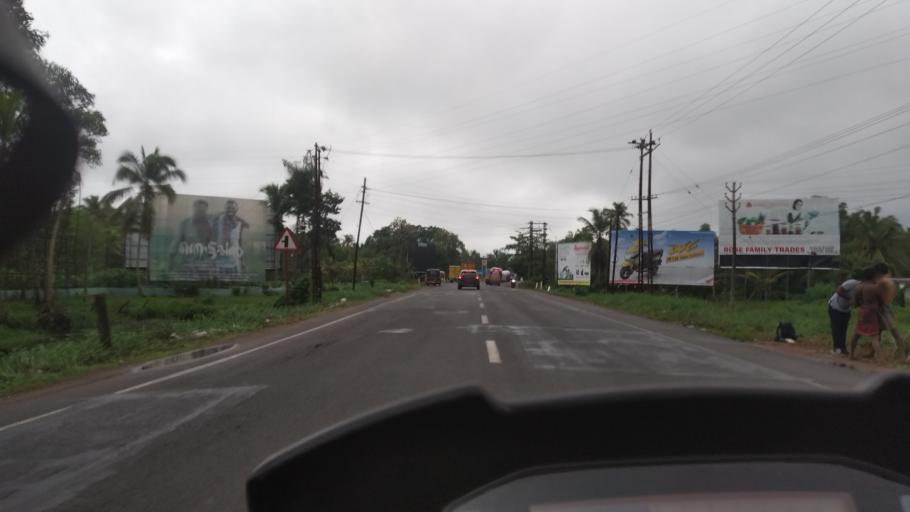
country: IN
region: Kerala
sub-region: Alappuzha
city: Mavelikara
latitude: 9.3169
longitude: 76.4176
